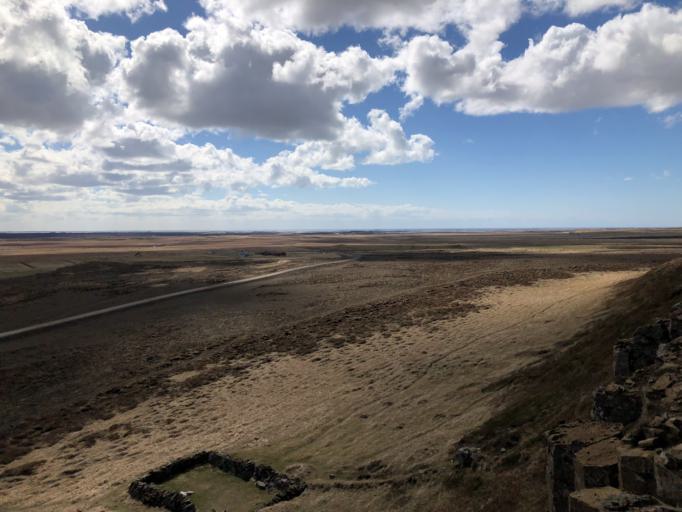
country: IS
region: West
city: Stykkisholmur
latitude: 64.8590
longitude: -22.3680
